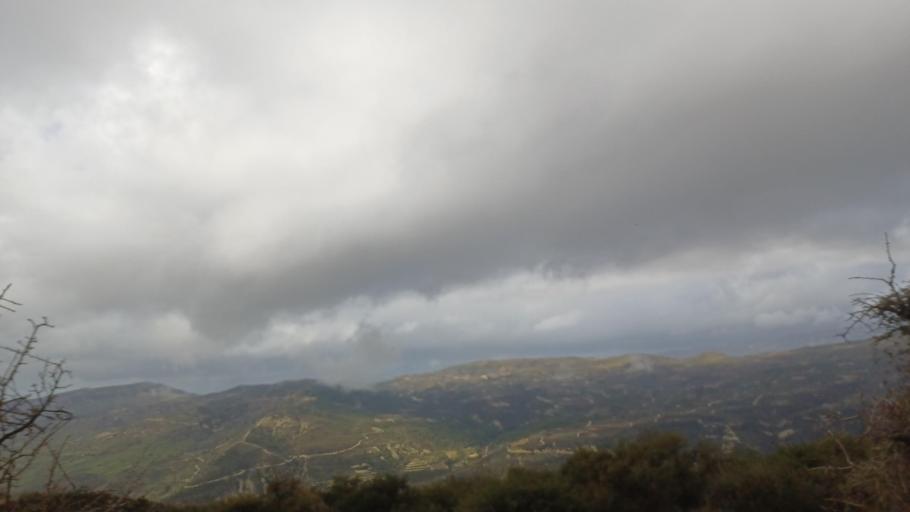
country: CY
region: Limassol
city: Pachna
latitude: 34.8337
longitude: 32.7439
